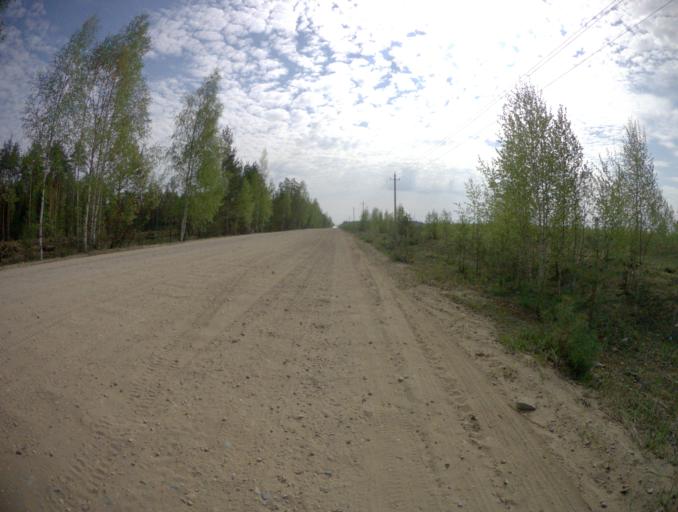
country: RU
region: Ivanovo
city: Yuzha
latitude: 56.5217
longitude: 42.0548
